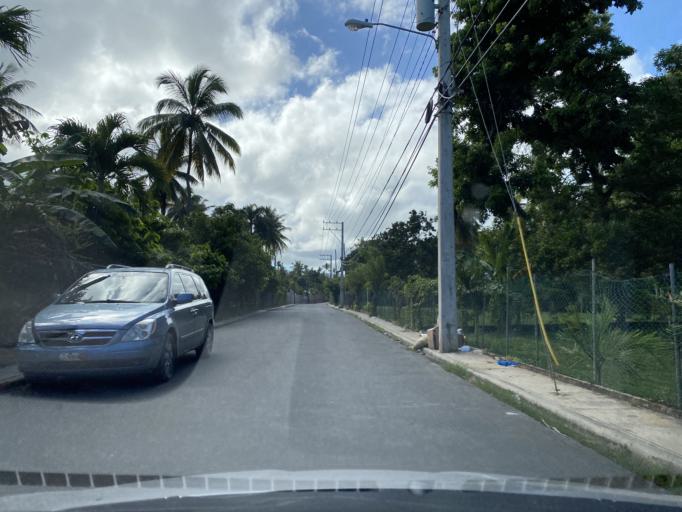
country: DO
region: Samana
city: Las Terrenas
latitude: 19.3112
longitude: -69.5473
